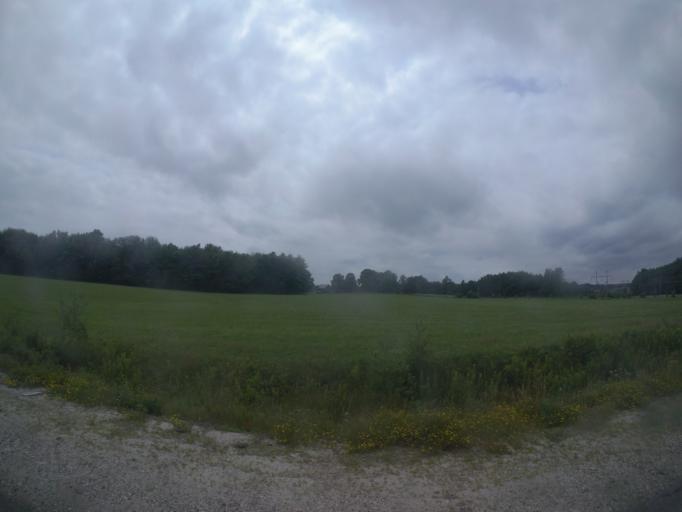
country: US
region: Maine
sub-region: Cumberland County
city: Cumberland Center
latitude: 43.7682
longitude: -70.2484
